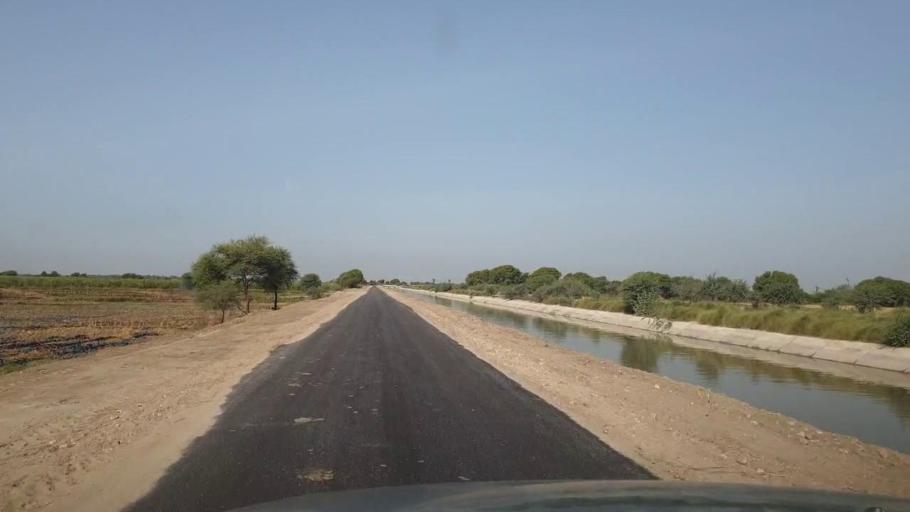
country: PK
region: Sindh
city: Tando Muhammad Khan
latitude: 25.1153
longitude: 68.3929
